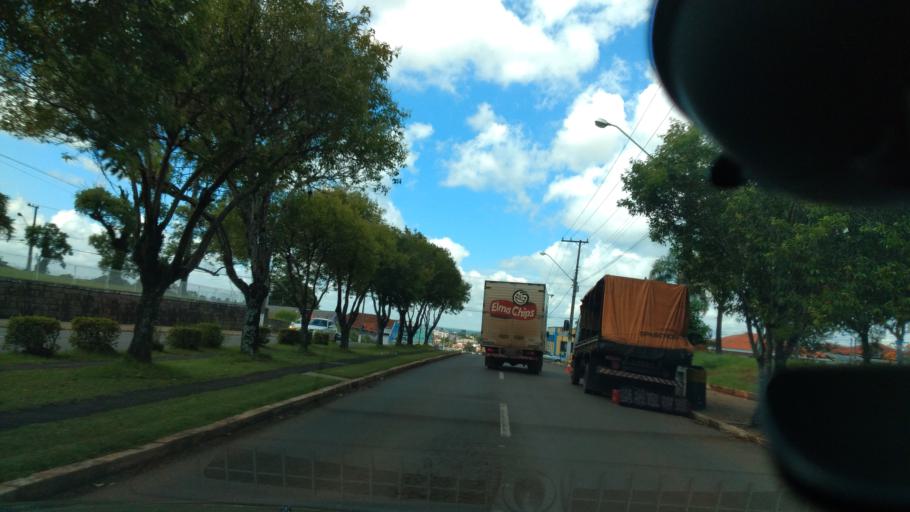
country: BR
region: Parana
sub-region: Guarapuava
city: Guarapuava
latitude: -25.3909
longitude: -51.4784
